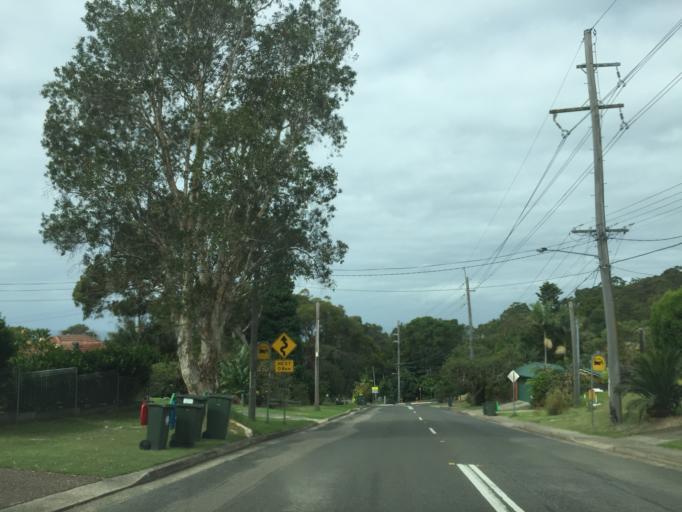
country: AU
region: New South Wales
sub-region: Pittwater
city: North Narrabeen
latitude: -33.7013
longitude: 151.2805
